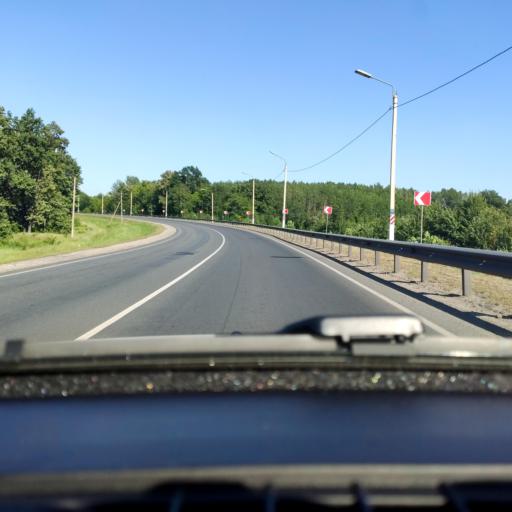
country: RU
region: Voronezj
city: Anna
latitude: 51.4902
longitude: 40.4573
